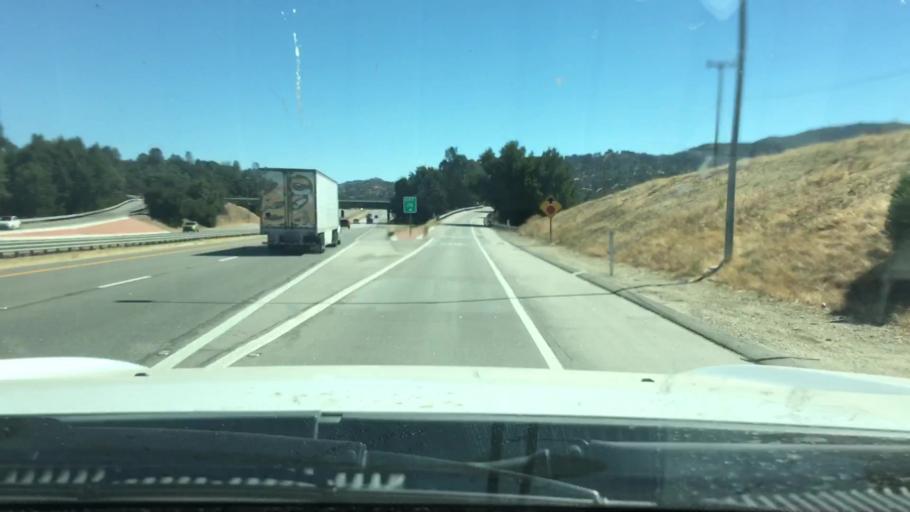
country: US
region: California
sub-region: San Luis Obispo County
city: Atascadero
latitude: 35.4519
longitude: -120.6408
